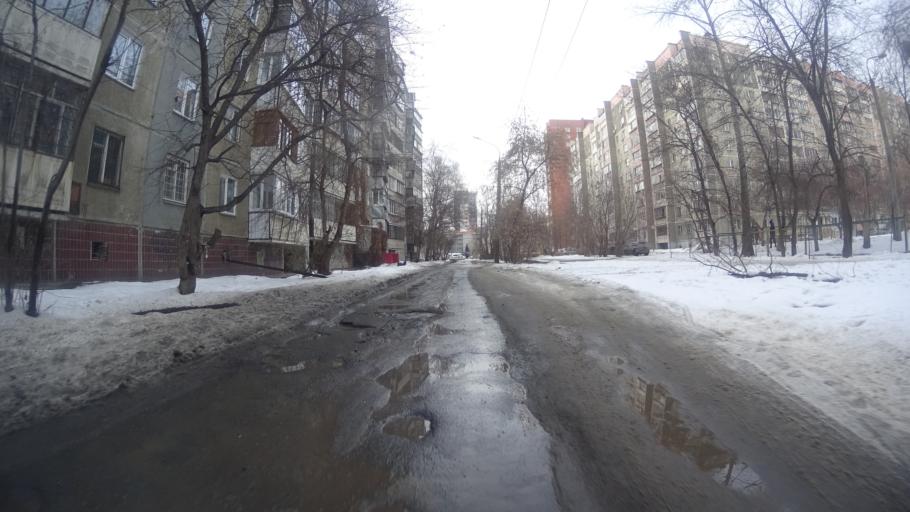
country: RU
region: Chelyabinsk
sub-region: Gorod Chelyabinsk
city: Chelyabinsk
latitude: 55.1764
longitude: 61.3472
